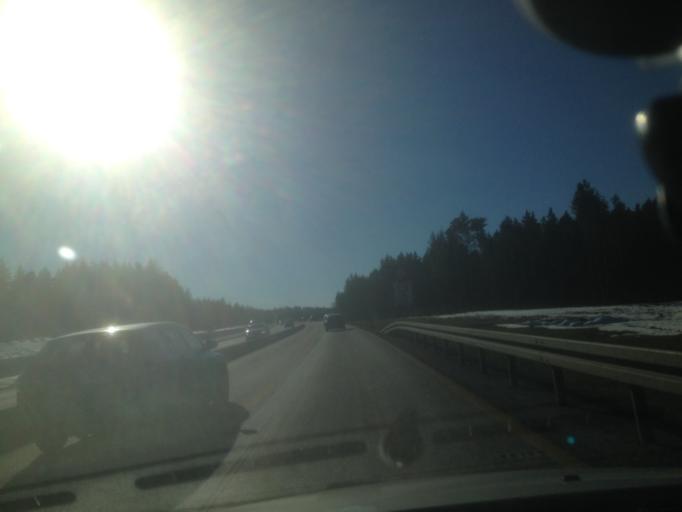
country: DE
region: Bavaria
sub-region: Swabia
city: Zusmarshausen
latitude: 48.4046
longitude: 10.5615
